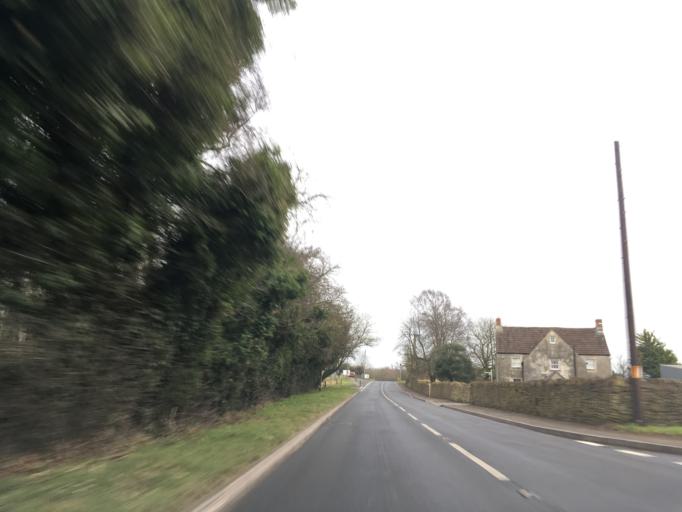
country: GB
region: England
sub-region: South Gloucestershire
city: Hinton
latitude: 51.5082
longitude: -2.3939
